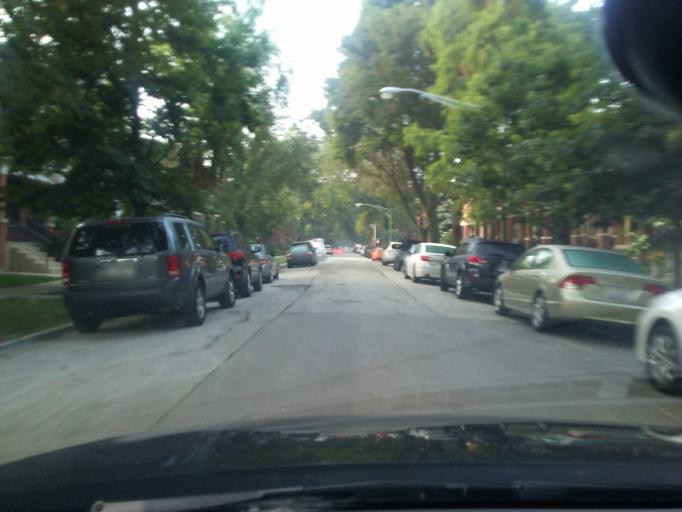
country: US
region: Illinois
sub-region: Cook County
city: Lincolnwood
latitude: 41.9498
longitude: -87.6847
